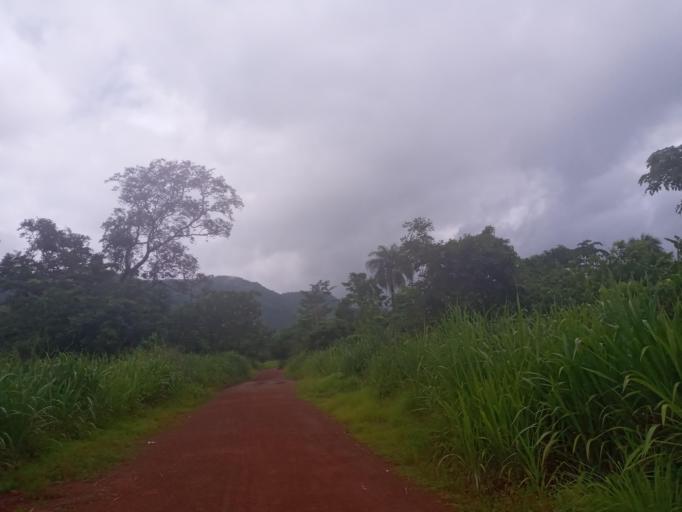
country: SL
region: Northern Province
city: Bumbuna
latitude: 8.9487
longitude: -11.7549
